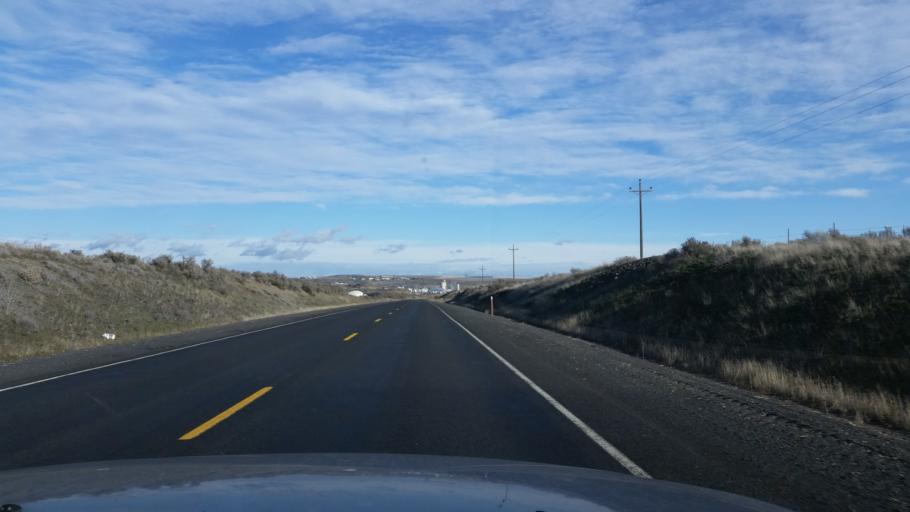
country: US
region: Washington
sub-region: Adams County
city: Ritzville
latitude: 47.3249
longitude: -118.7219
